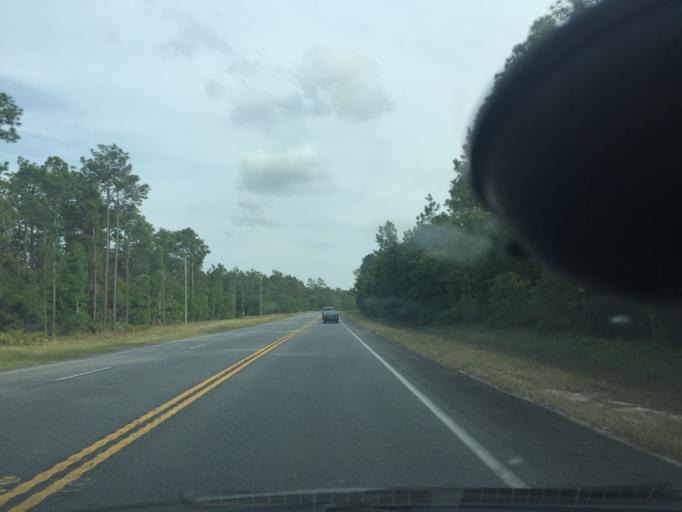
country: US
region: Georgia
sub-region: Chatham County
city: Bloomingdale
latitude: 32.0433
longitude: -81.3325
